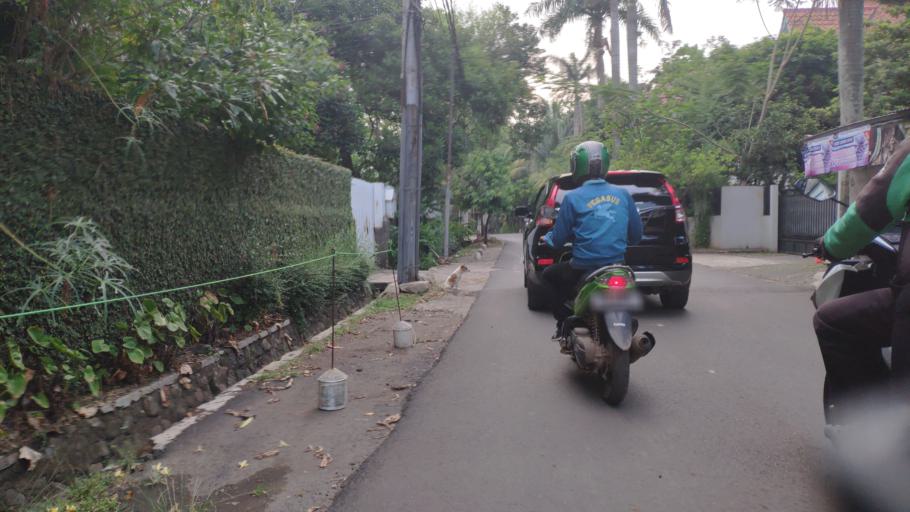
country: ID
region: West Java
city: Pamulang
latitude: -6.2949
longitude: 106.8008
